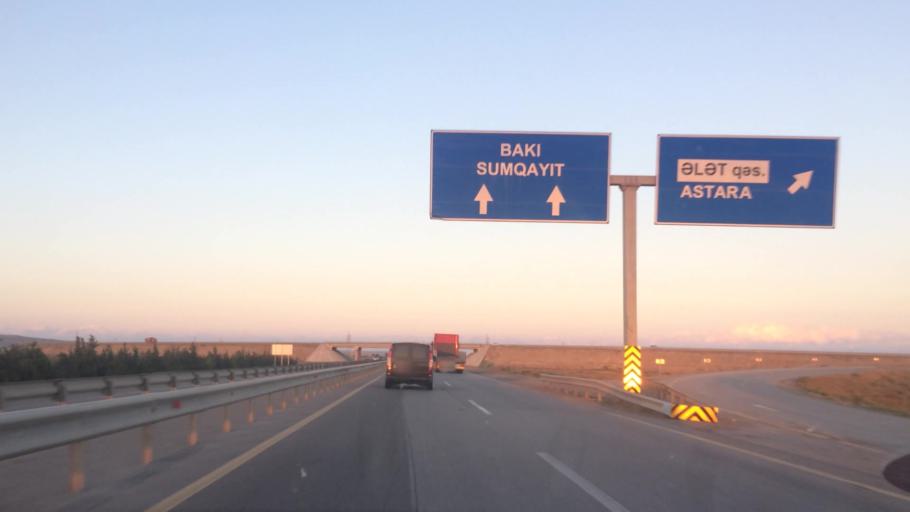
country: AZ
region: Baki
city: Qobustan
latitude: 39.9524
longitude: 49.3747
